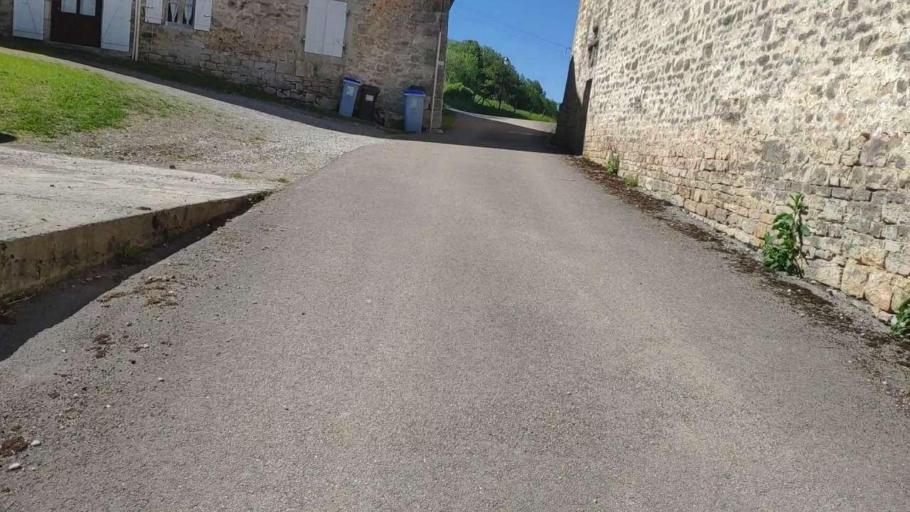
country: FR
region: Franche-Comte
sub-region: Departement du Jura
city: Clairvaux-les-Lacs
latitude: 46.7001
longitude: 5.7325
